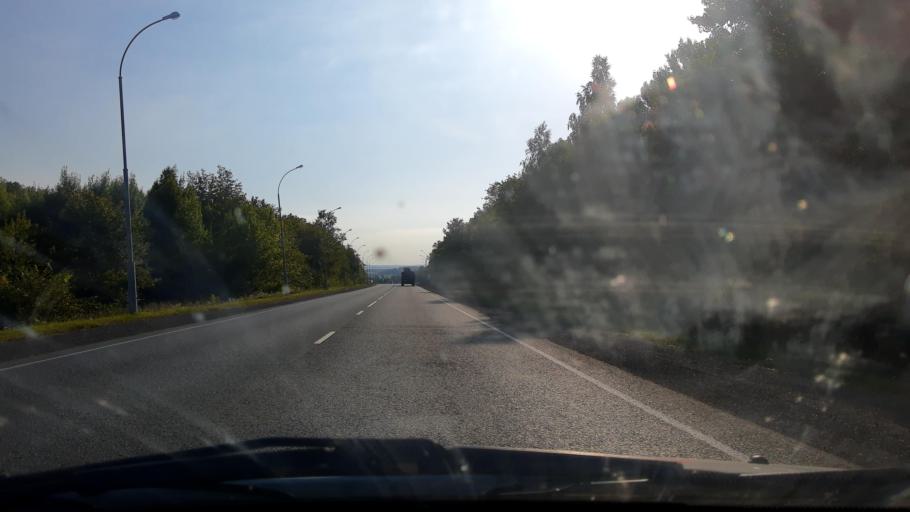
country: RU
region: Bashkortostan
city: Oktyabr'skiy
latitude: 54.4477
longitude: 53.5854
